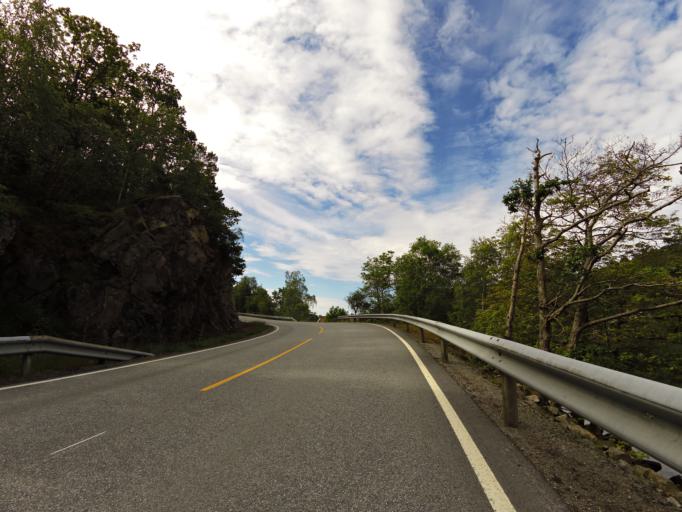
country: NO
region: Vest-Agder
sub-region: Lindesnes
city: Vigeland
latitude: 58.0573
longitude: 7.1810
